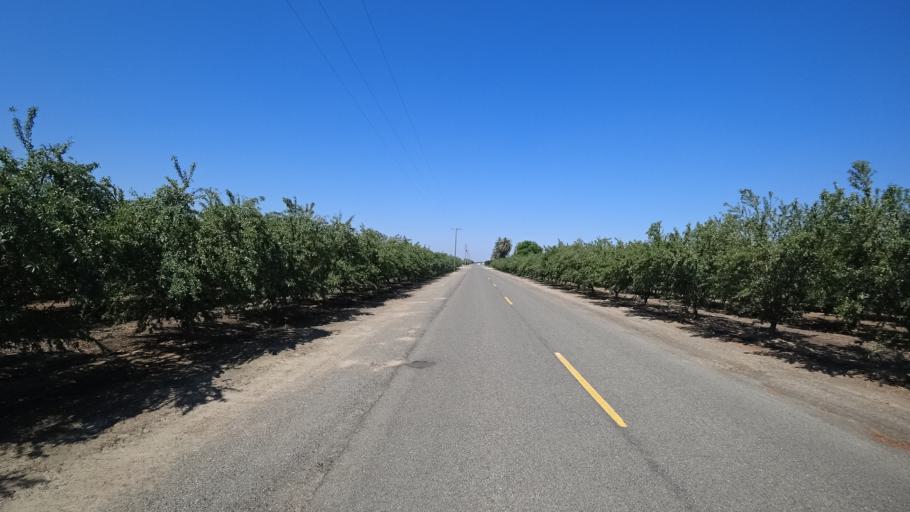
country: US
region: California
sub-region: Fresno County
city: Kingsburg
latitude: 36.4668
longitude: -119.5538
